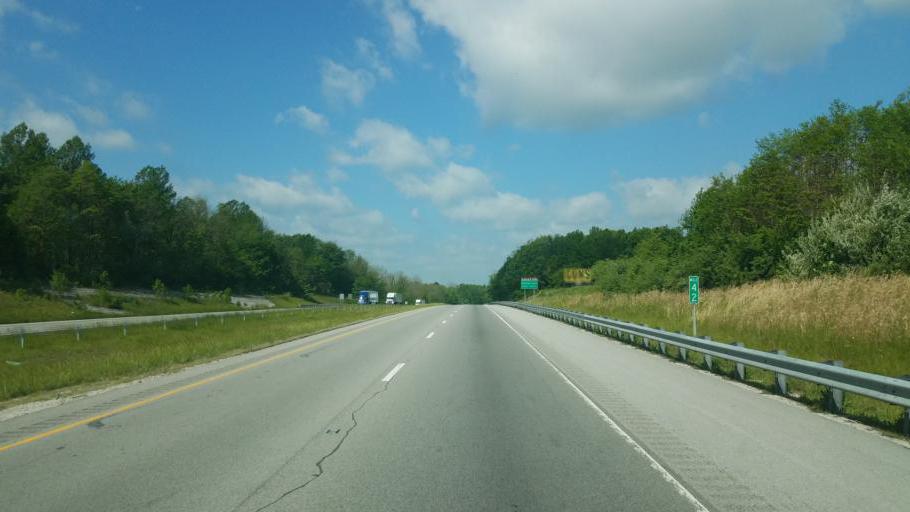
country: US
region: Indiana
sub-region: Putnam County
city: Cloverdale
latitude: 39.5340
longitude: -86.7871
